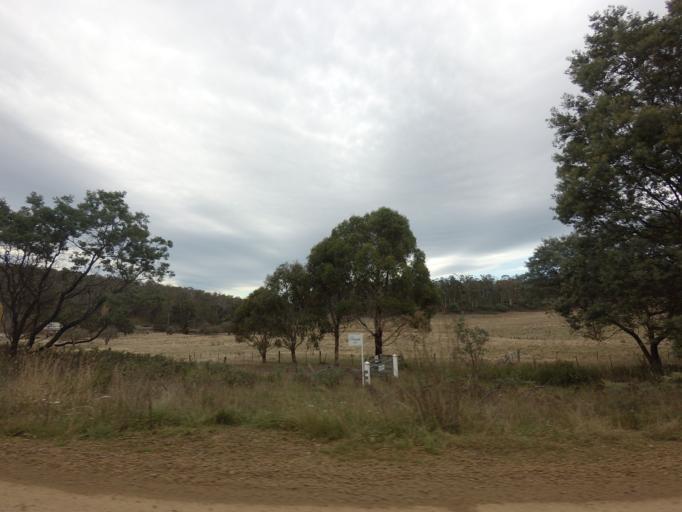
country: AU
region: Tasmania
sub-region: Derwent Valley
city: New Norfolk
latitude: -42.5609
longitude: 146.9511
